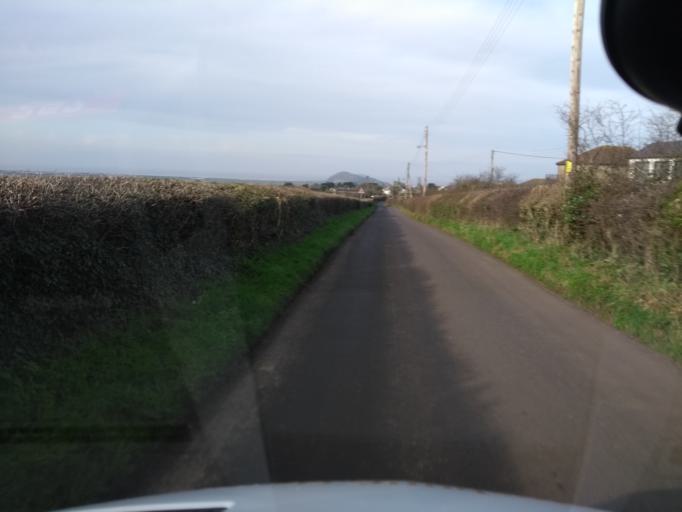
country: GB
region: England
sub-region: North Somerset
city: Bleadon
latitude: 51.3151
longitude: -2.9541
